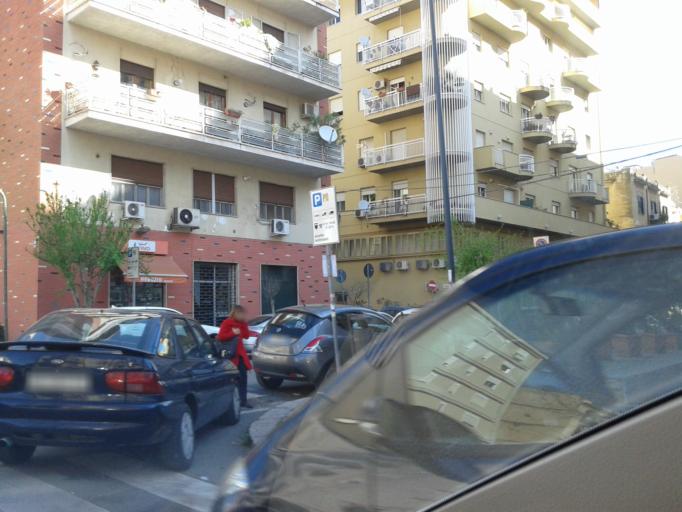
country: IT
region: Sicily
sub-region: Palermo
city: Palermo
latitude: 38.1342
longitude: 13.3458
